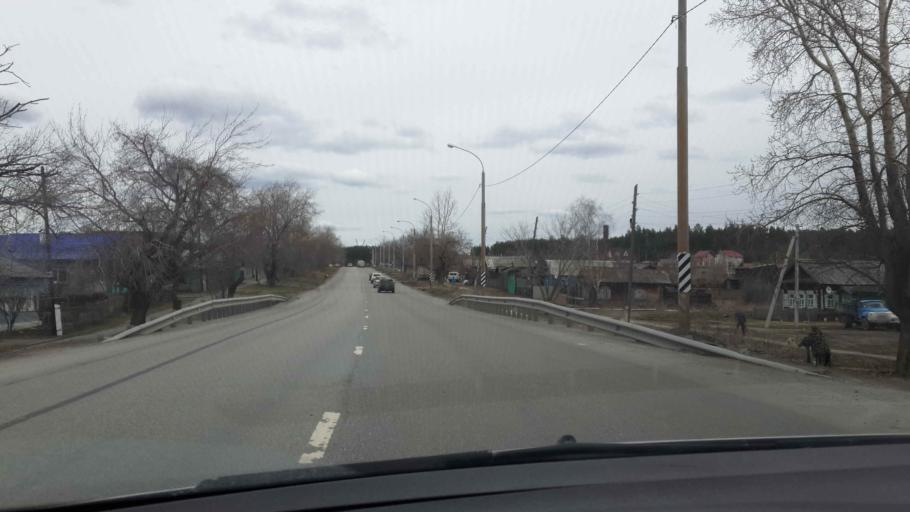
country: RU
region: Sverdlovsk
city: Beloyarskiy
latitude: 56.7670
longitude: 61.4294
